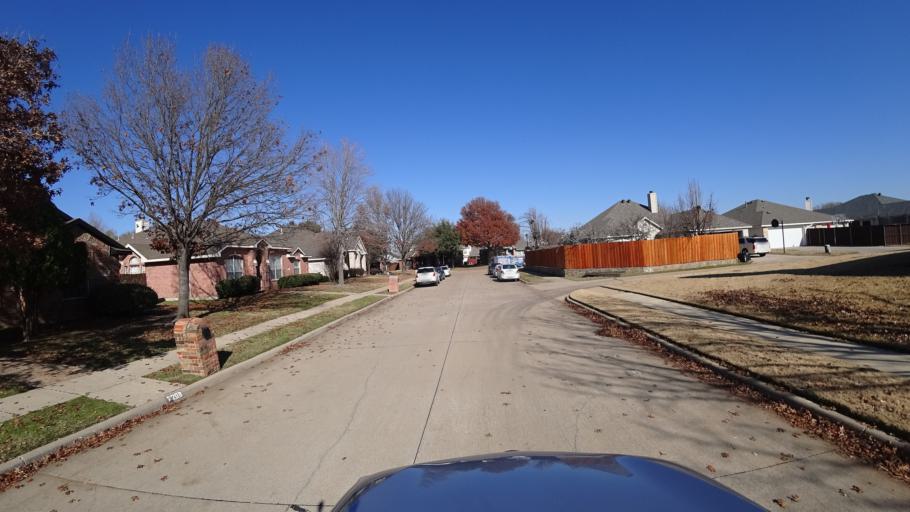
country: US
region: Texas
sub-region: Denton County
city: Lewisville
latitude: 33.0096
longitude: -97.0251
